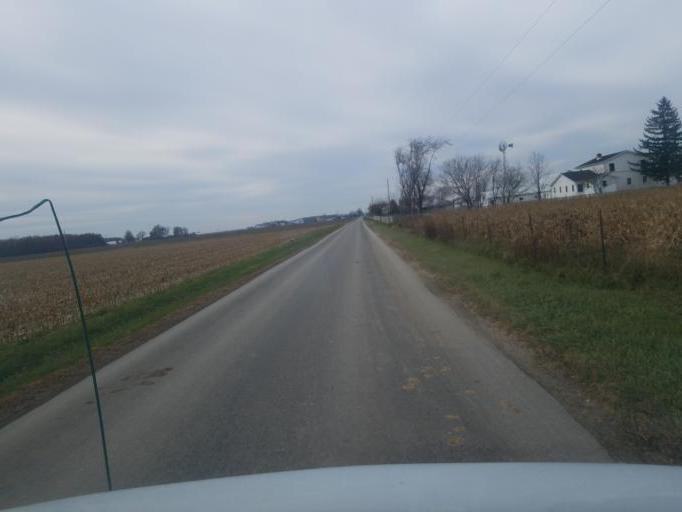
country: US
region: Indiana
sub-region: Adams County
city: Geneva
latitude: 40.6152
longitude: -84.8568
